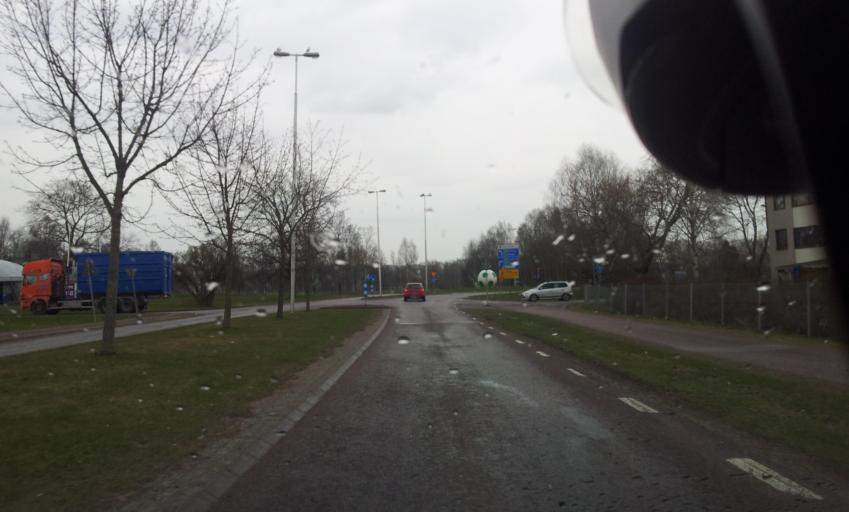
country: SE
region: Dalarna
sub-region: Borlange Kommun
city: Borlaenge
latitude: 60.4944
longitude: 15.4007
